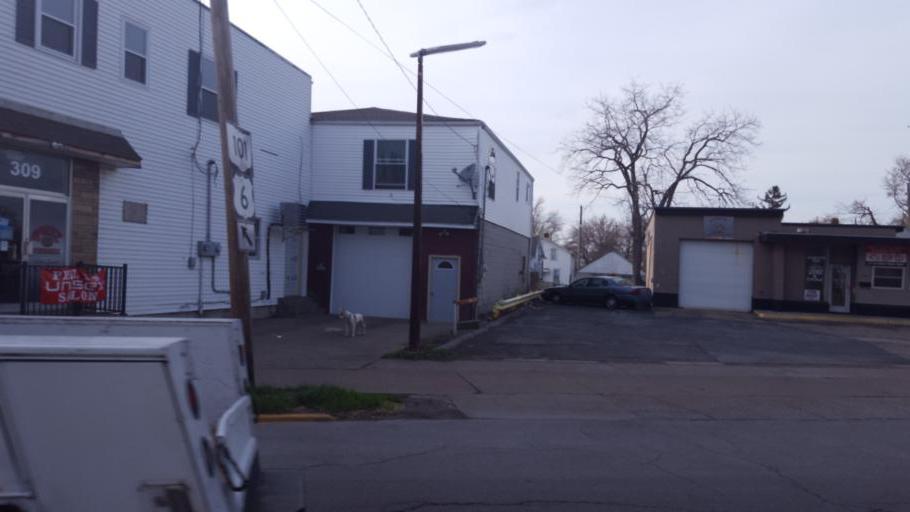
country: US
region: Ohio
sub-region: Erie County
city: Sandusky
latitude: 41.4516
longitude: -82.7211
